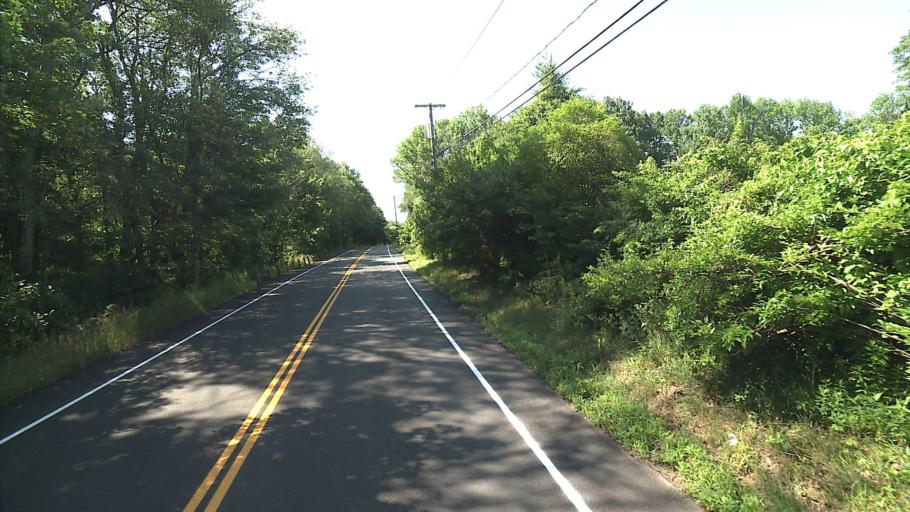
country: US
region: Connecticut
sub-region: Litchfield County
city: Northwest Harwinton
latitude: 41.7706
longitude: -73.0259
